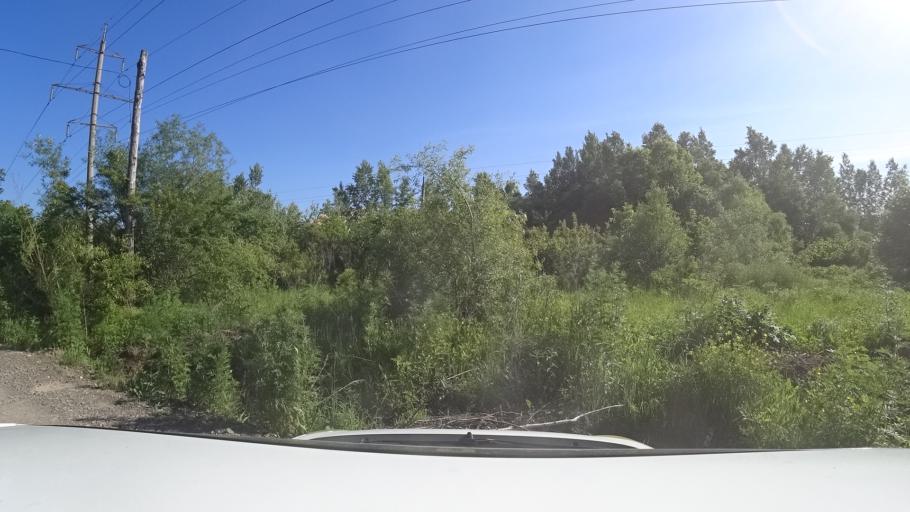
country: RU
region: Khabarovsk Krai
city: Topolevo
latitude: 48.5420
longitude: 135.1707
